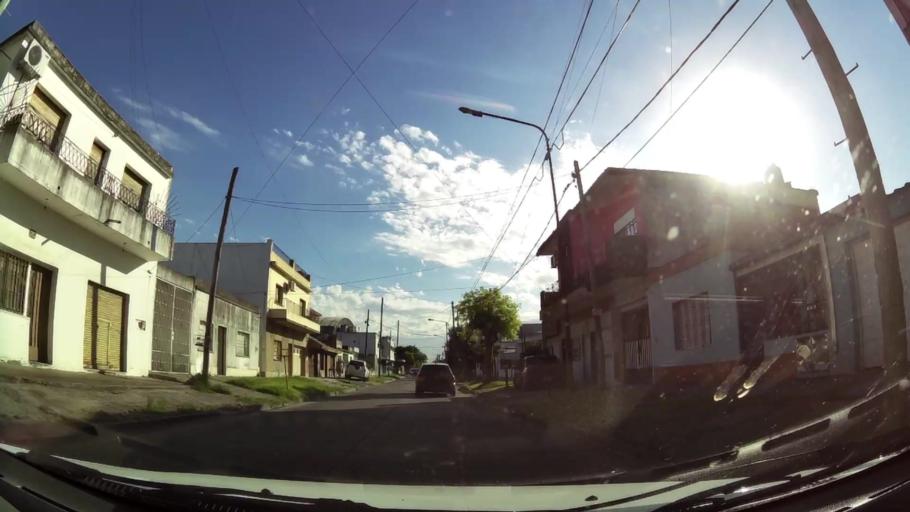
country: AR
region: Buenos Aires
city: Hurlingham
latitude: -34.5640
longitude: -58.6165
